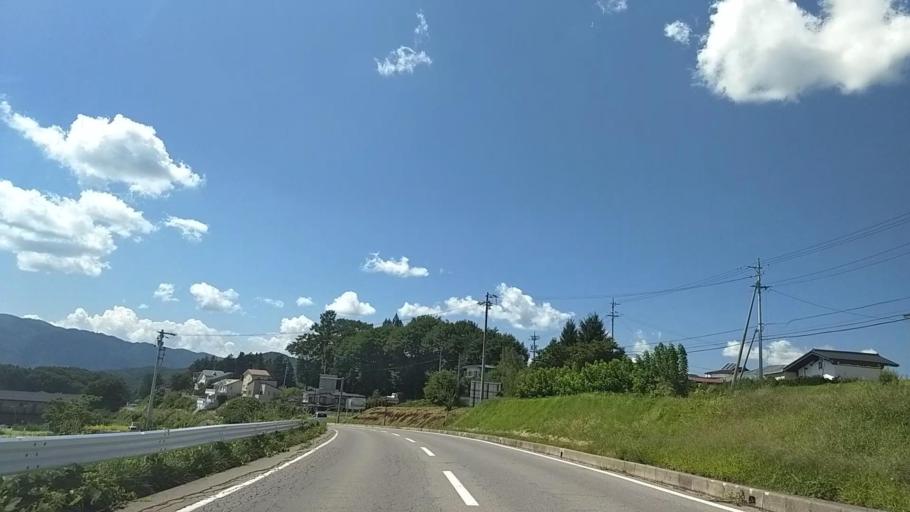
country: JP
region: Nagano
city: Chino
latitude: 36.0208
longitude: 138.2030
